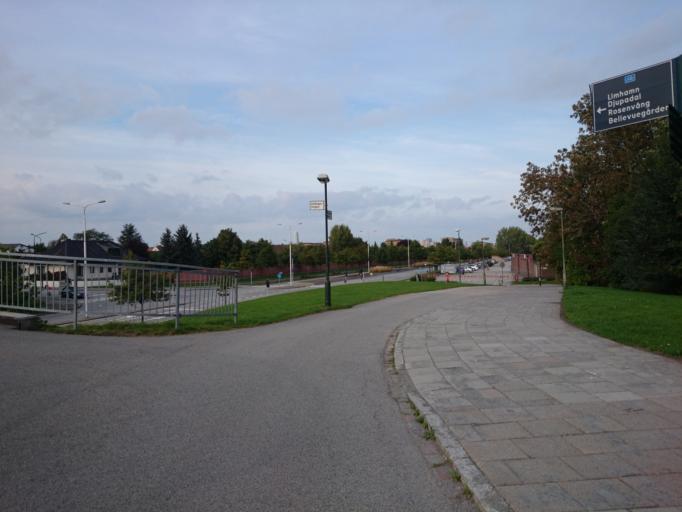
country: SE
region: Skane
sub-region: Malmo
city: Malmoe
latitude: 55.5758
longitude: 12.9731
